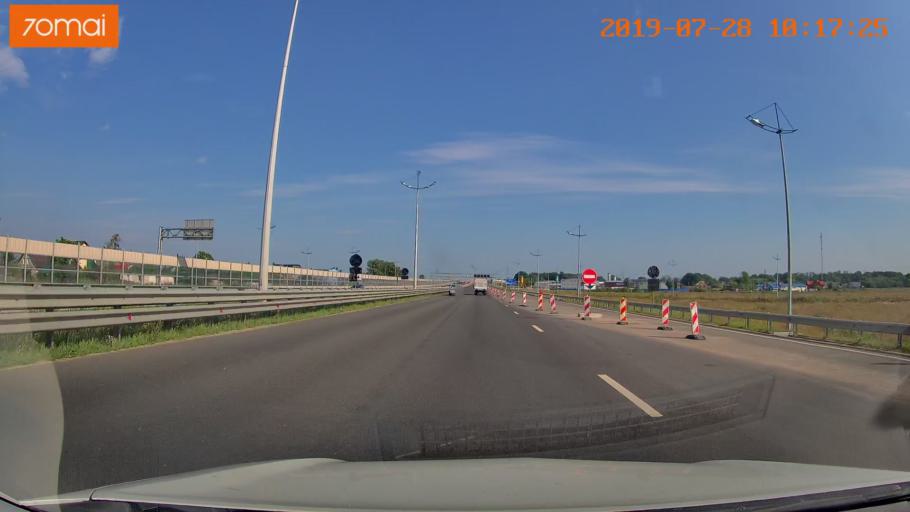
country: RU
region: Kaliningrad
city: Maloye Isakovo
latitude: 54.7396
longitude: 20.5945
